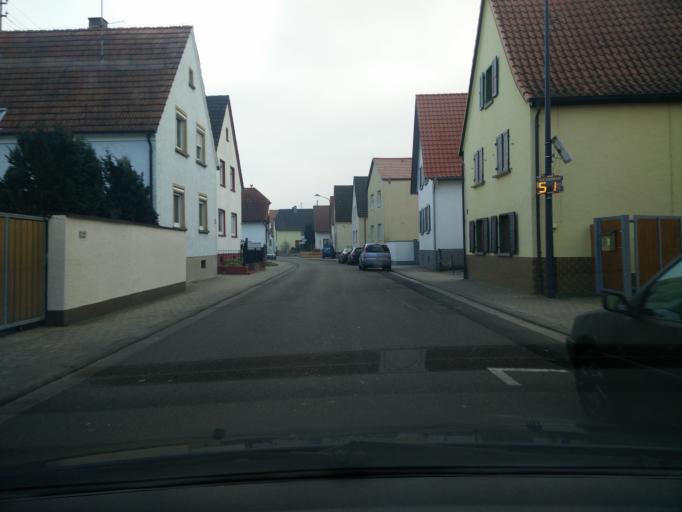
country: DE
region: Rheinland-Pfalz
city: Minfeld
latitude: 49.0734
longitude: 8.1667
